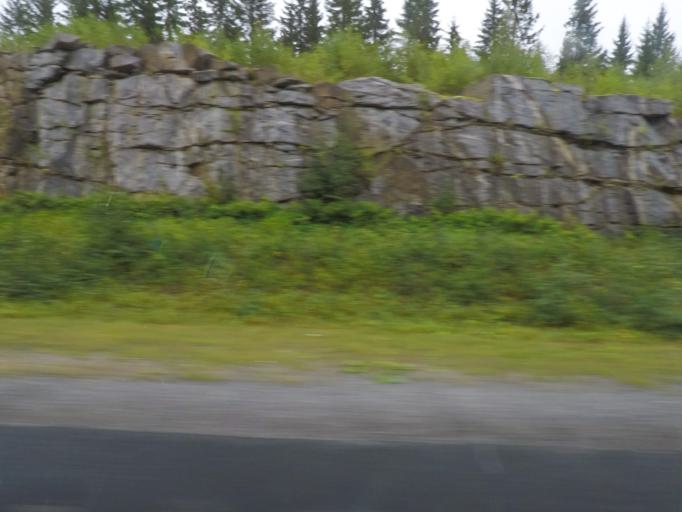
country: FI
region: Northern Savo
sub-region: Kuopio
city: Kuopio
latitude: 62.7292
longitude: 27.5852
